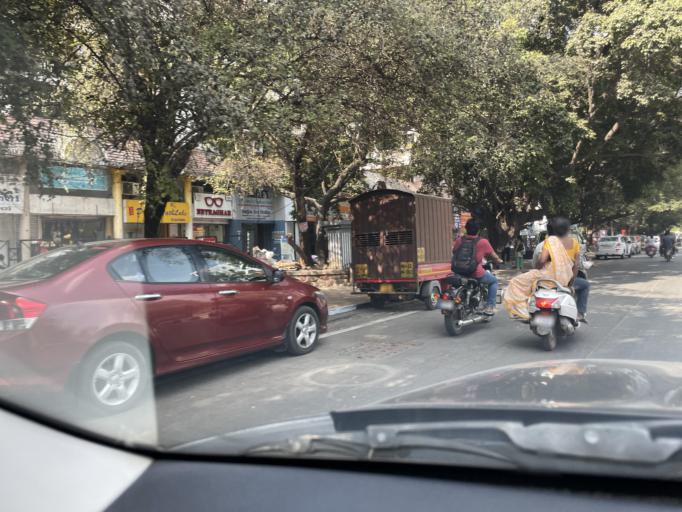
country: IN
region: Maharashtra
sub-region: Pune Division
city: Pune
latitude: 18.4903
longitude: 73.9000
